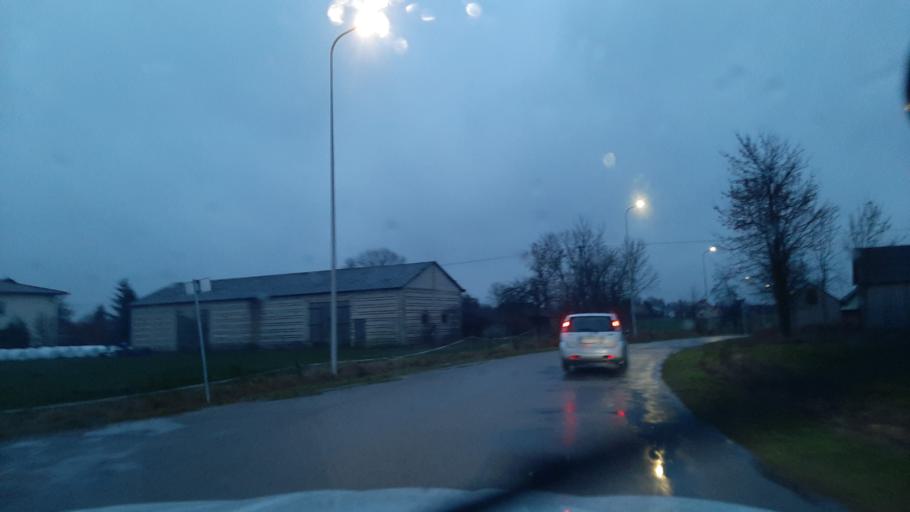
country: PL
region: Lublin Voivodeship
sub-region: Powiat lubelski
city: Jastkow
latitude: 51.3639
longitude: 22.4546
